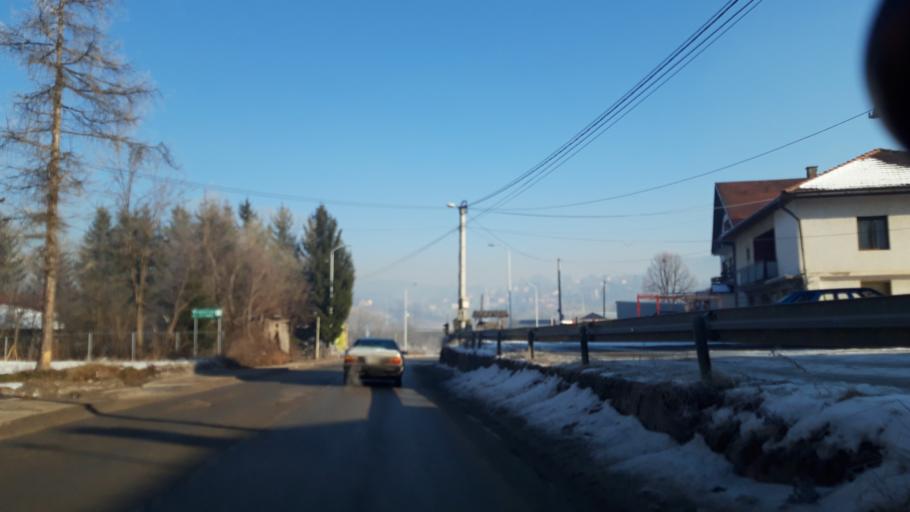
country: BA
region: Republika Srpska
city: Pale
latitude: 43.8156
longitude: 18.5590
